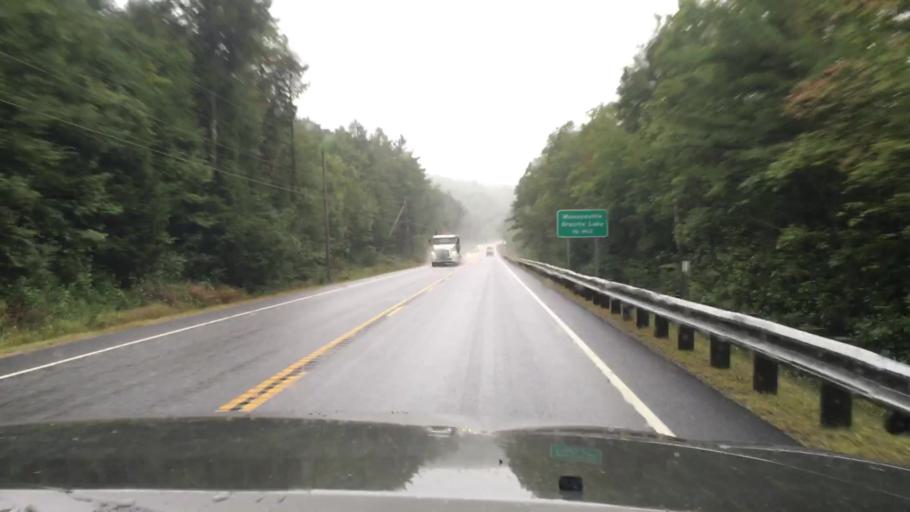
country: US
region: New Hampshire
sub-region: Cheshire County
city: Harrisville
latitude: 43.0281
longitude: -72.1216
